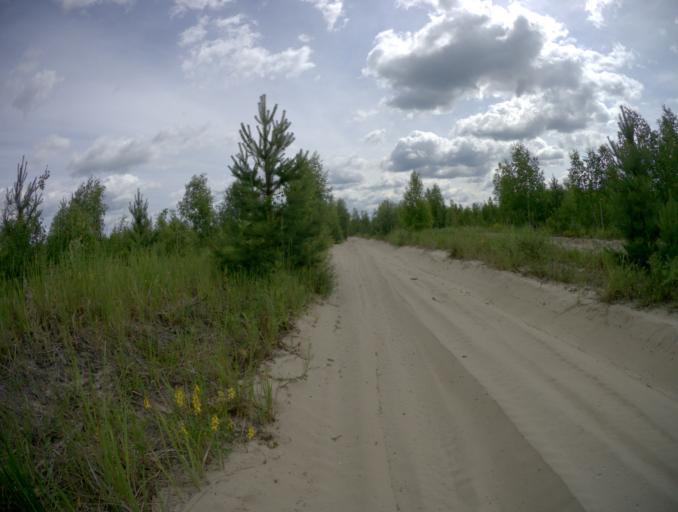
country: RU
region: Nizjnij Novgorod
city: Frolishchi
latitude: 56.4976
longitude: 42.5680
